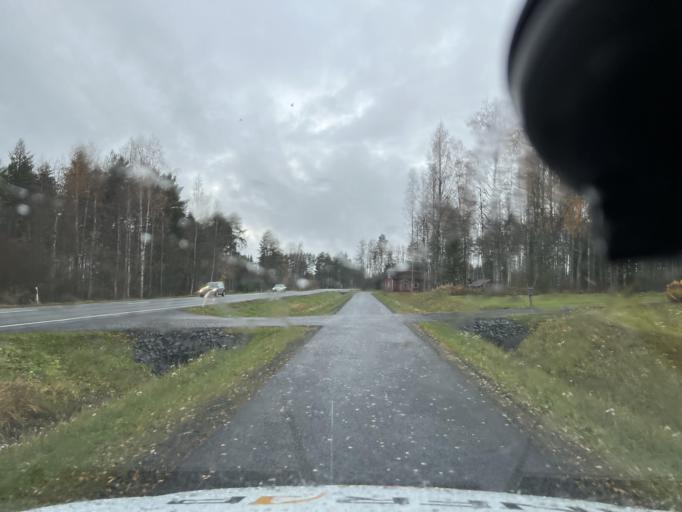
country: FI
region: Northern Ostrobothnia
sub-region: Ylivieska
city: Sievi
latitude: 63.9624
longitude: 24.5021
